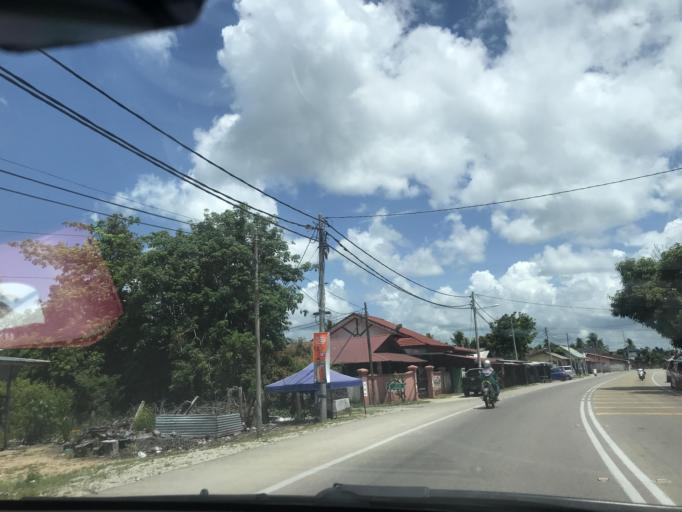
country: TH
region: Narathiwat
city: Tak Bai
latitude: 6.2228
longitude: 102.1074
